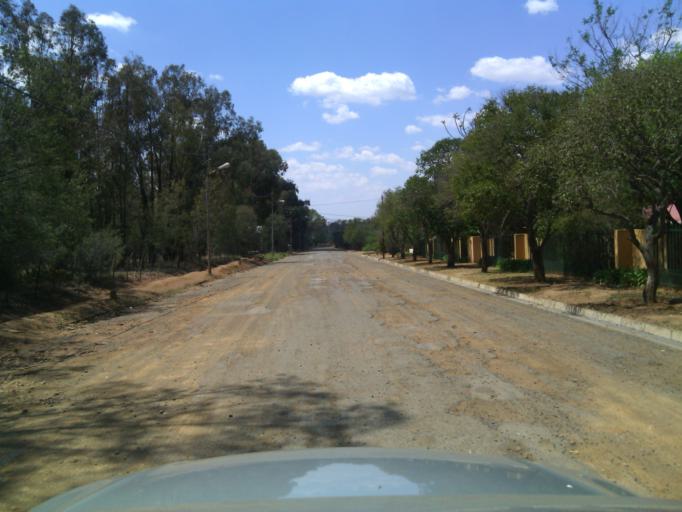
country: ZA
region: Orange Free State
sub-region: Xhariep District Municipality
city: Dewetsdorp
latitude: -29.5784
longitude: 26.6636
